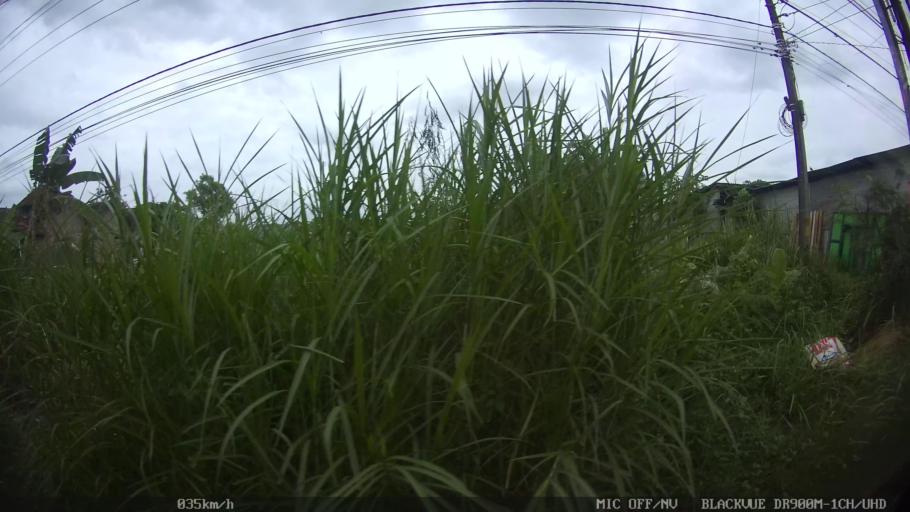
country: ID
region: Daerah Istimewa Yogyakarta
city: Sewon
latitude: -7.8307
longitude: 110.4127
